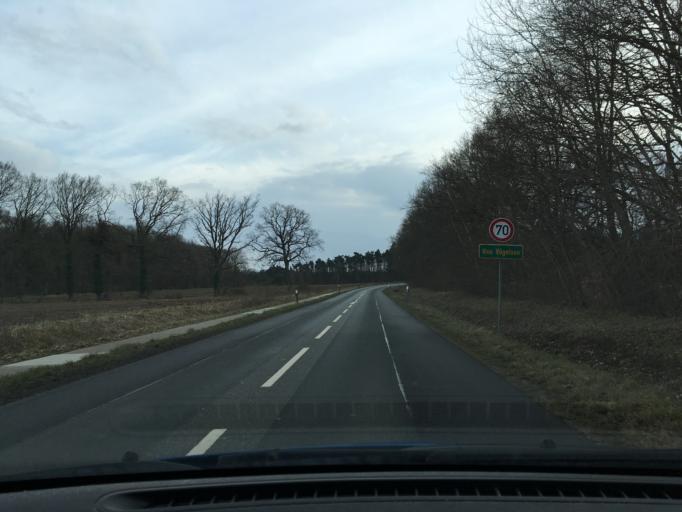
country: DE
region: Lower Saxony
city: Reppenstedt
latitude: 53.2638
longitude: 10.3403
